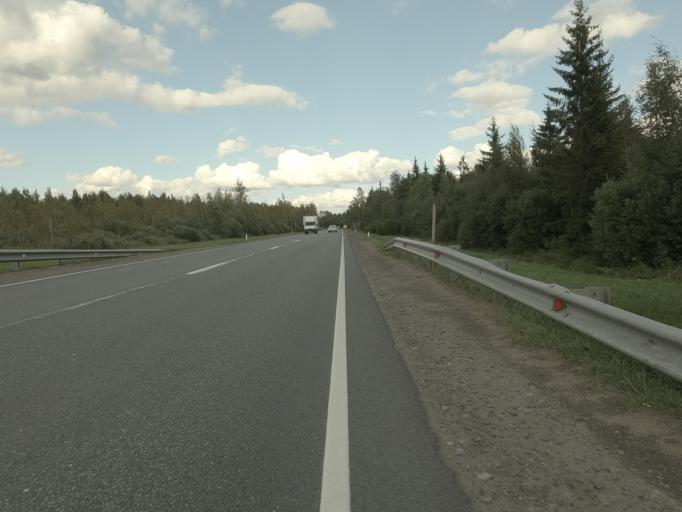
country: RU
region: Leningrad
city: Pavlovo
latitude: 59.6783
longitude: 30.9388
